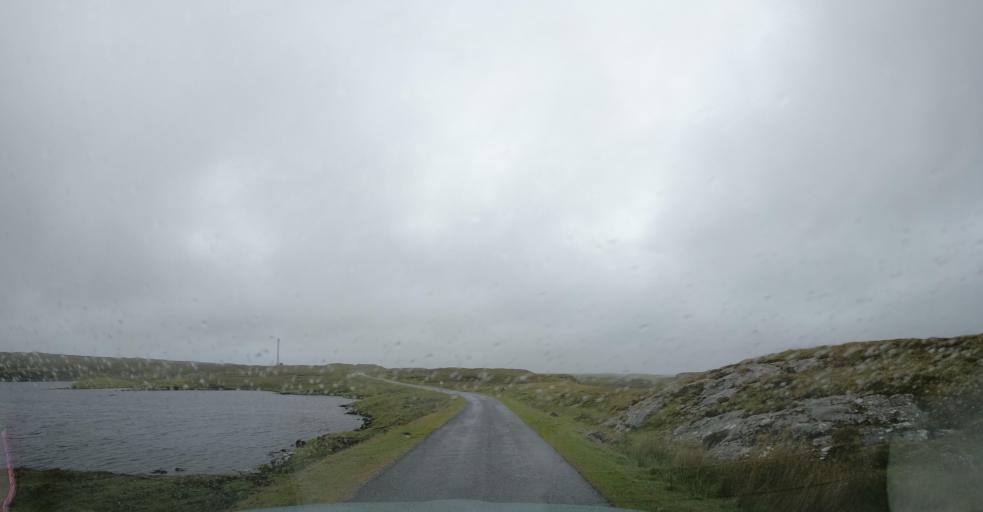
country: GB
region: Scotland
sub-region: Eilean Siar
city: Benbecula
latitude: 57.4931
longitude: -7.2269
